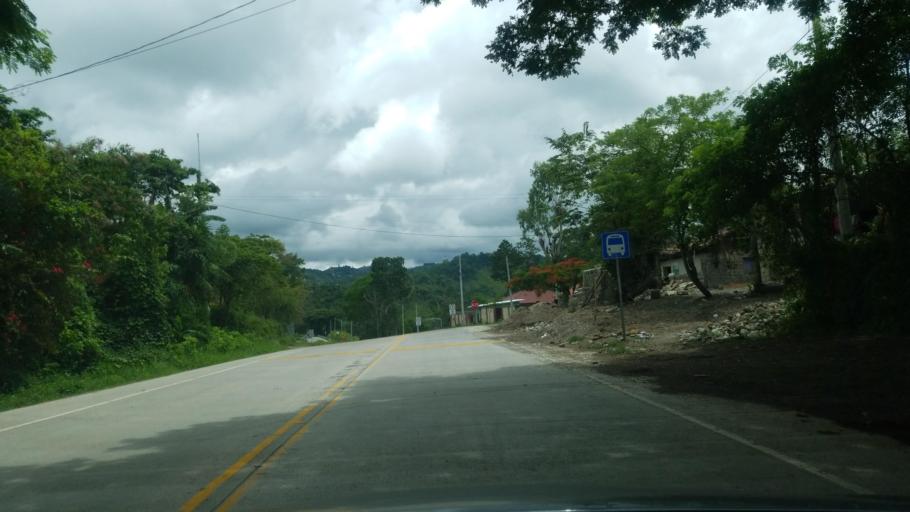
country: HN
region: Copan
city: San Jeronimo
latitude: 14.9845
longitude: -88.8668
